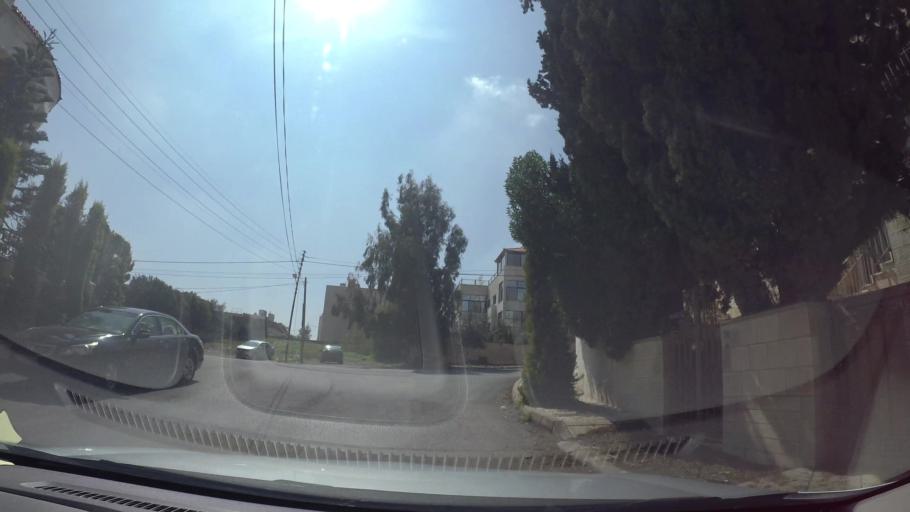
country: JO
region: Amman
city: Al Bunayyat ash Shamaliyah
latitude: 31.8975
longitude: 35.8878
